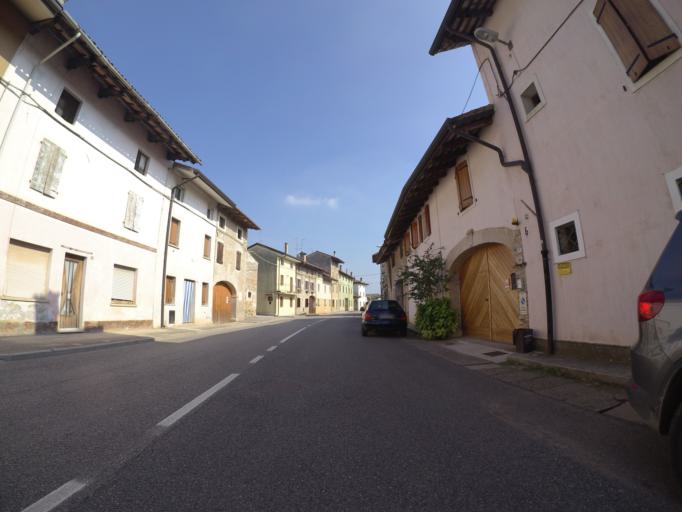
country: IT
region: Friuli Venezia Giulia
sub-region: Provincia di Udine
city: Basiliano
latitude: 45.9959
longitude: 13.0270
